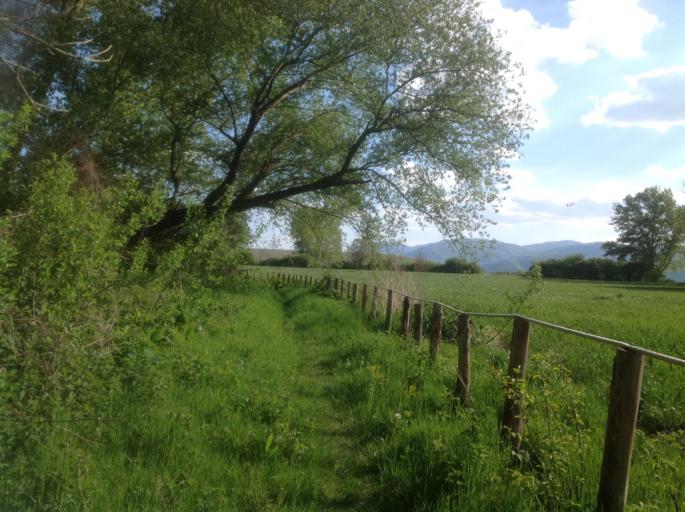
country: IT
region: Latium
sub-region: Provincia di Rieti
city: Colli sul Velino
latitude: 42.4703
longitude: 12.8056
